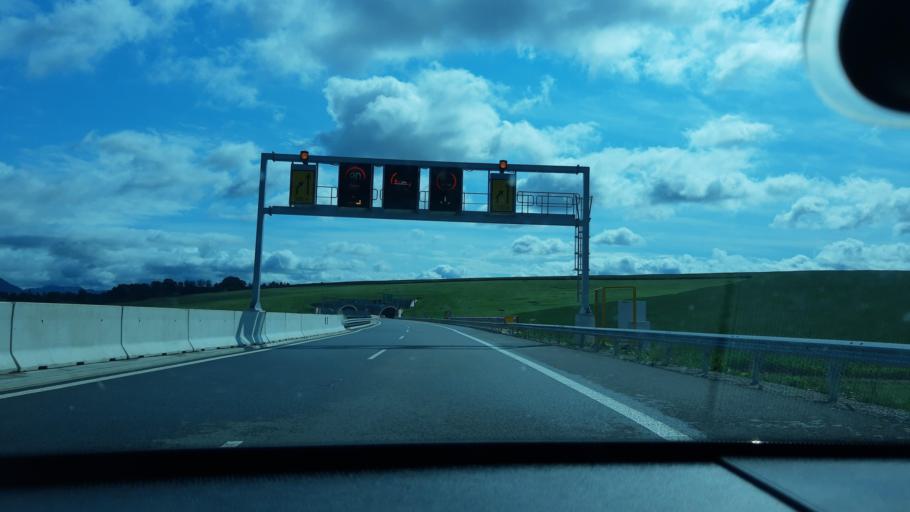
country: SK
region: Zilinsky
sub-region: Okres Zilina
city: Zilina
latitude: 49.1885
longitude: 18.7053
